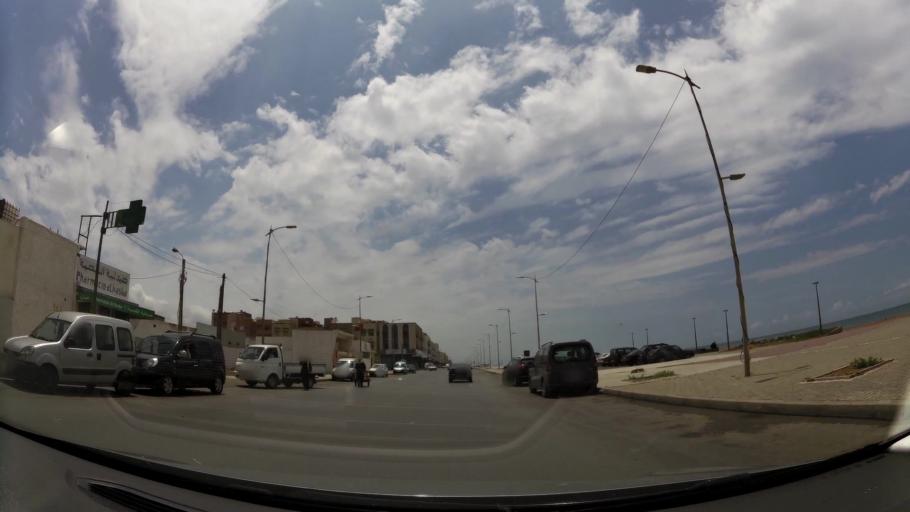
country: MA
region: Rabat-Sale-Zemmour-Zaer
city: Sale
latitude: 34.0566
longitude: -6.8199
